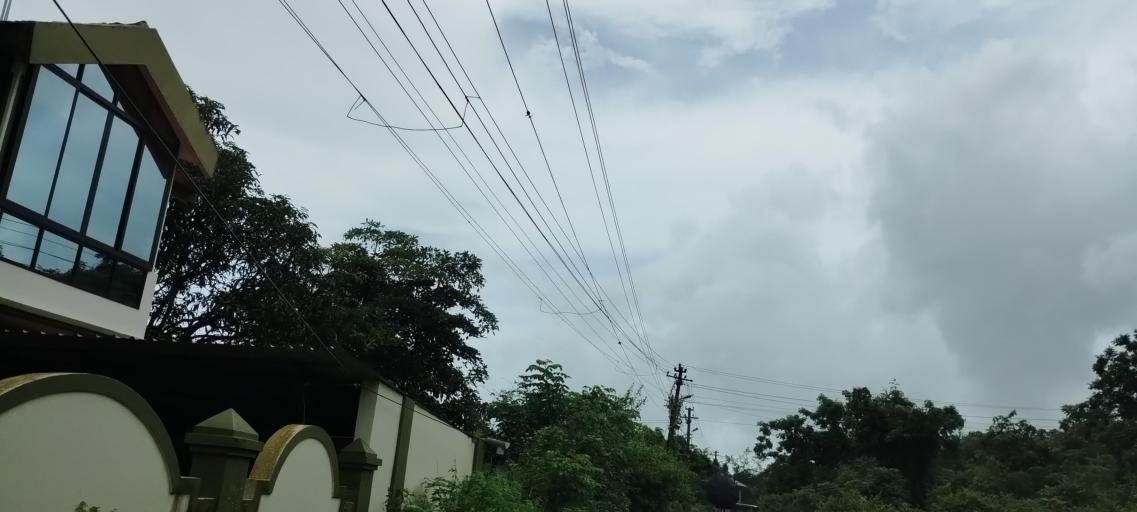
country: IN
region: Goa
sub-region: North Goa
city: Aldona
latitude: 15.5827
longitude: 73.8668
